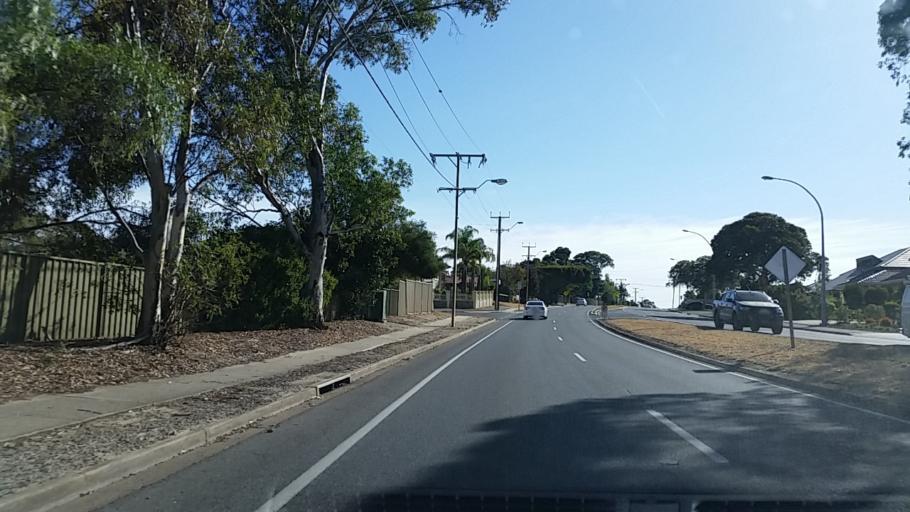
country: AU
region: South Australia
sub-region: Campbelltown
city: Athelstone
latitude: -34.8525
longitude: 138.7084
